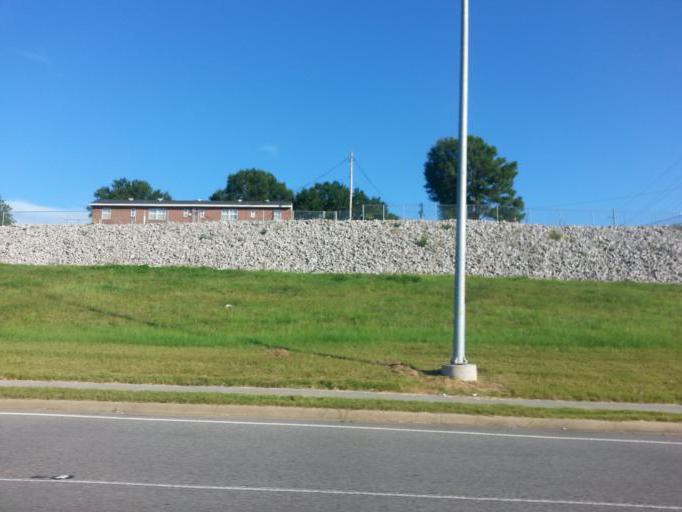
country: US
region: Alabama
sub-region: Lauderdale County
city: East Florence
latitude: 34.8161
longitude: -87.6625
